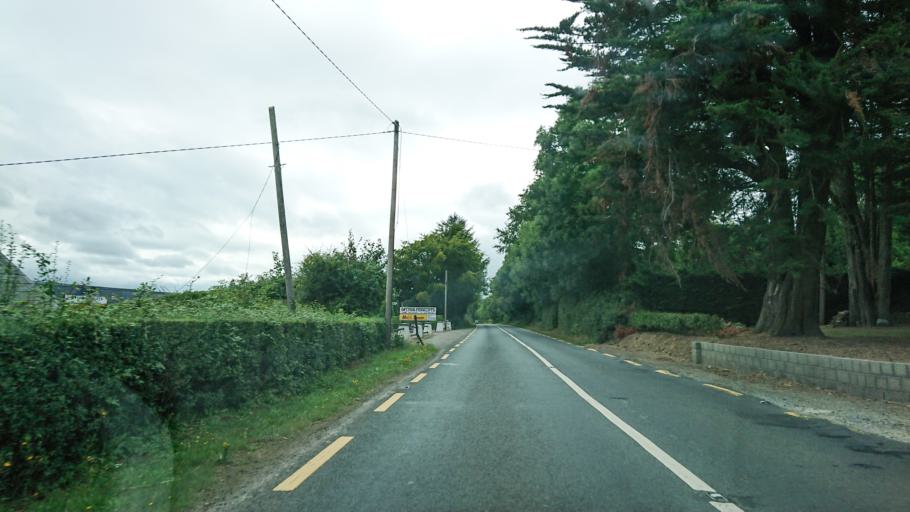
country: IE
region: Munster
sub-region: County Cork
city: Kanturk
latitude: 52.1442
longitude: -8.8730
